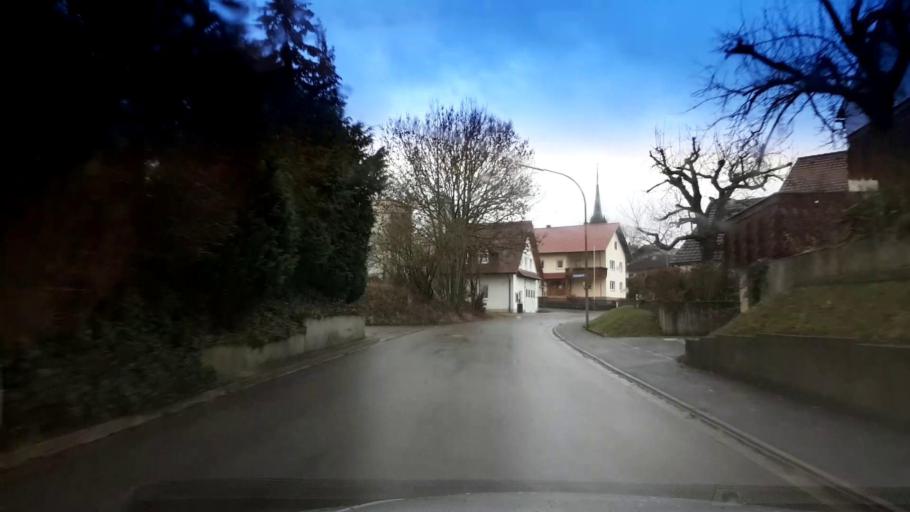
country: DE
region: Bavaria
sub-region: Upper Franconia
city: Litzendorf
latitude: 49.8733
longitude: 11.0448
